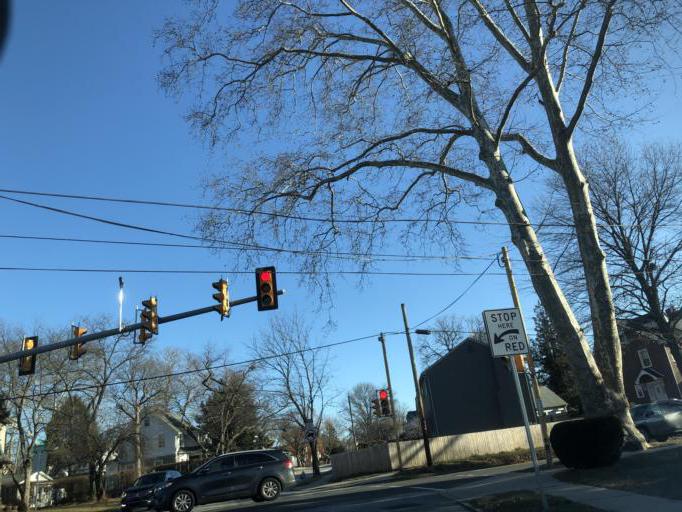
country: US
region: Pennsylvania
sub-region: Delaware County
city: Drexel Hill
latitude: 39.9459
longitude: -75.3007
